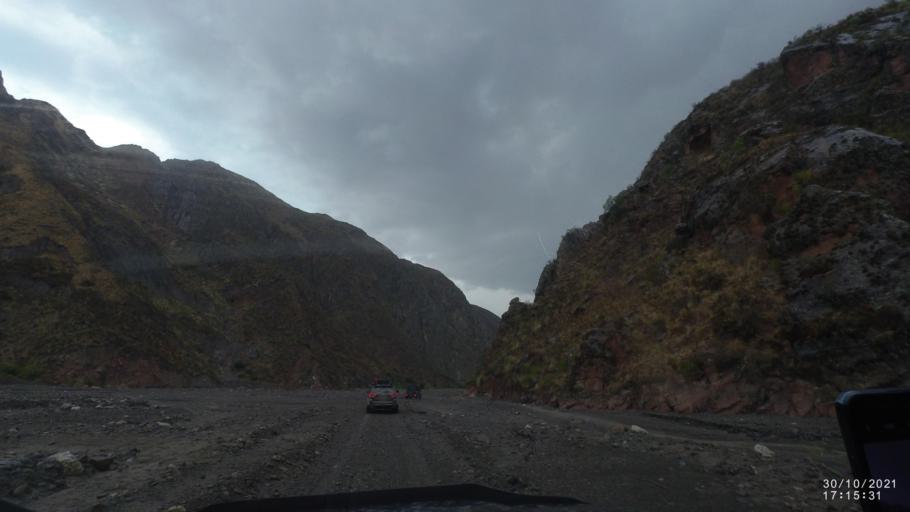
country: BO
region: Cochabamba
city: Colchani
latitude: -17.5434
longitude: -66.6274
